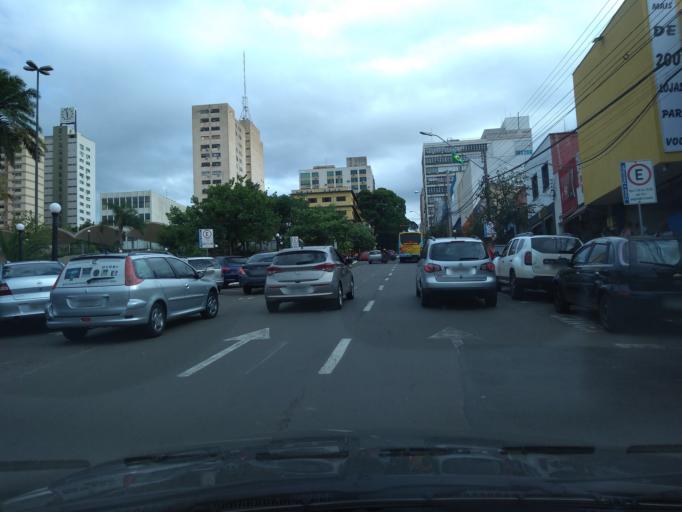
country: BR
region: Parana
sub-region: Londrina
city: Londrina
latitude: -23.3089
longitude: -51.1602
